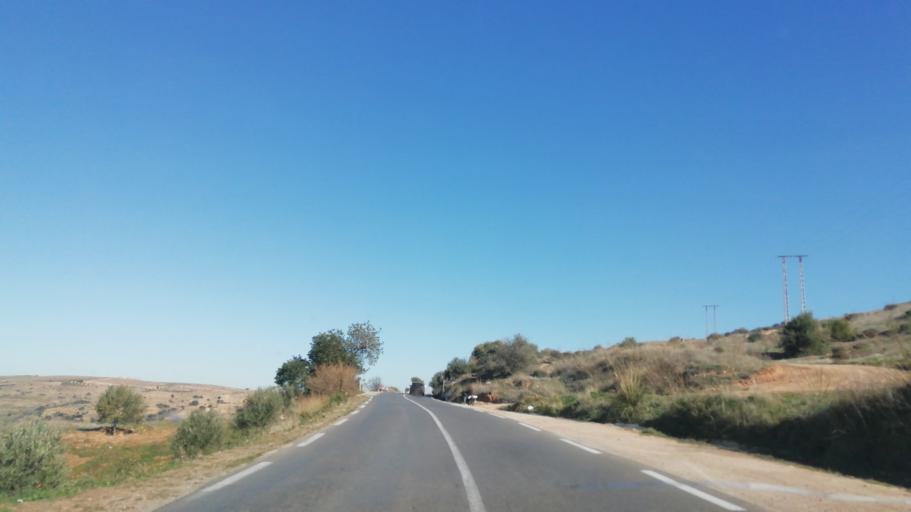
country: DZ
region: Tlemcen
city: Beni Mester
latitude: 34.8386
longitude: -1.4889
